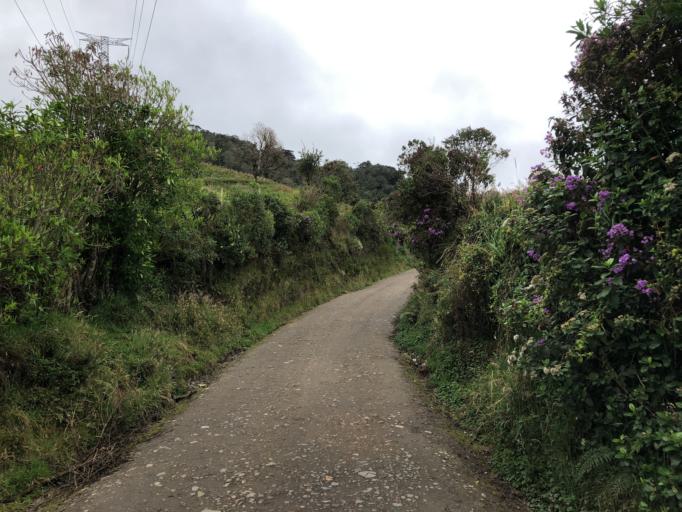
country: CO
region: Cauca
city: Totoro
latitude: 2.4977
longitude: -76.3497
